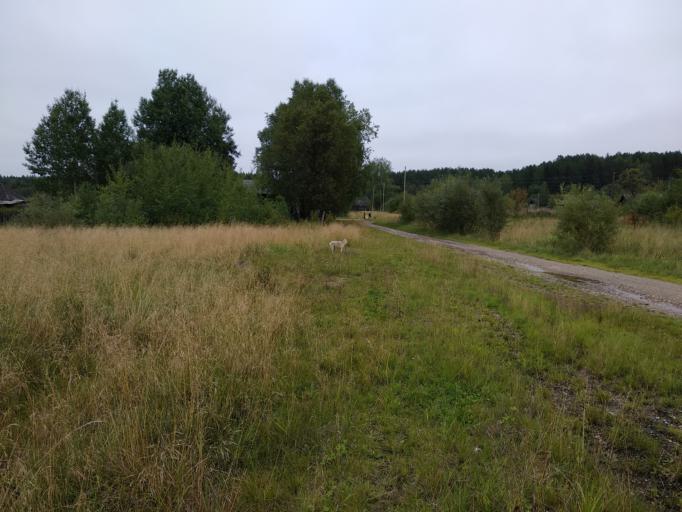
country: RU
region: Sverdlovsk
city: Serov
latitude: 59.8447
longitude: 60.7251
